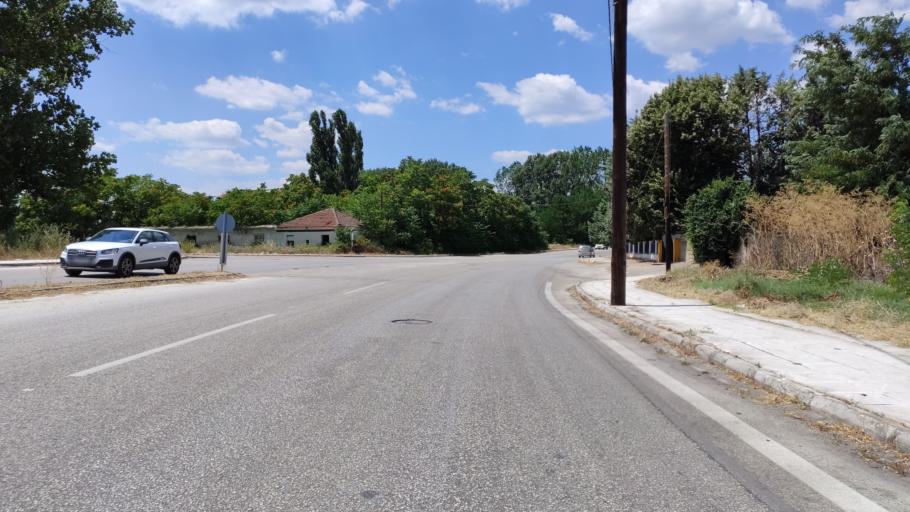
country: GR
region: East Macedonia and Thrace
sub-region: Nomos Rodopis
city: Komotini
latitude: 41.1265
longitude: 25.3870
